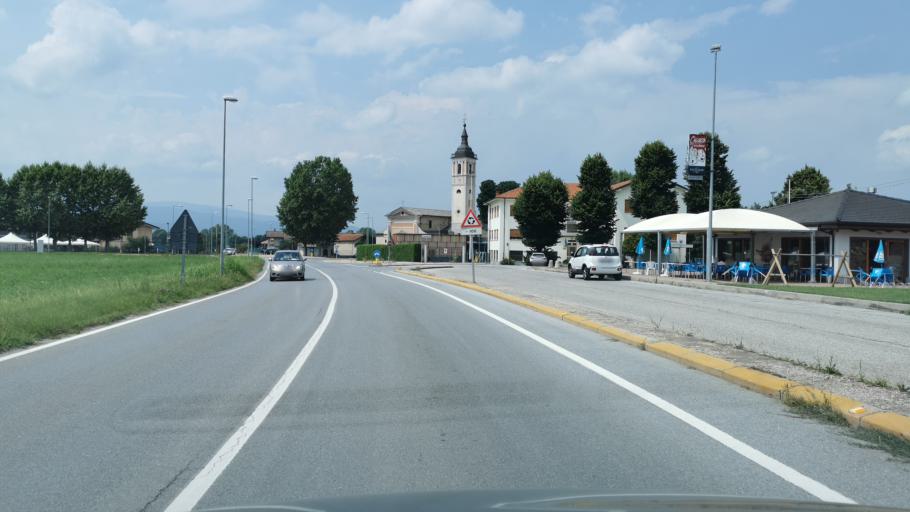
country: IT
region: Piedmont
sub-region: Provincia di Cuneo
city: Roata Rossi
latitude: 44.4315
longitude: 7.5061
